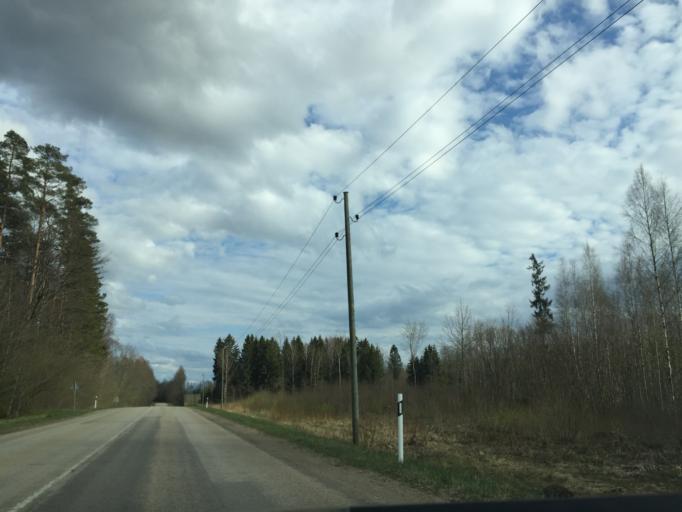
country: LV
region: Aluksnes Rajons
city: Aluksne
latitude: 57.4406
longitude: 26.9620
